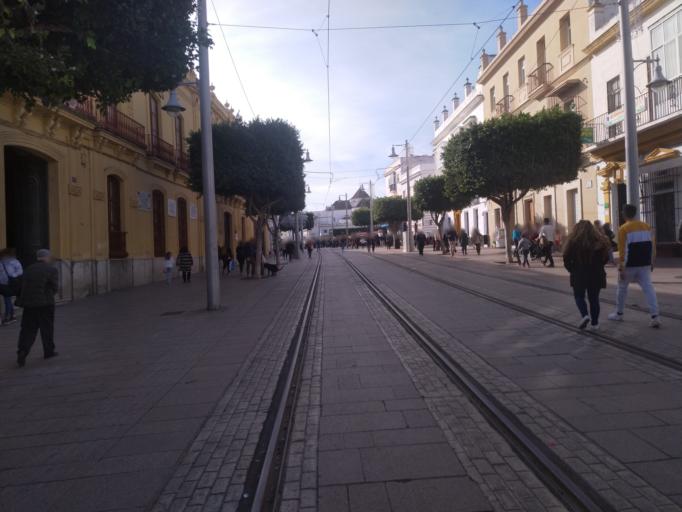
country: ES
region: Andalusia
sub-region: Provincia de Cadiz
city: San Fernando
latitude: 36.4644
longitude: -6.1993
